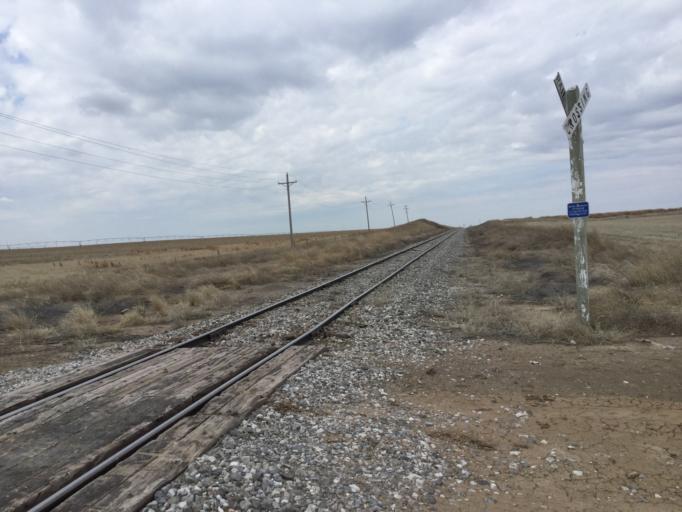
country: US
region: Kansas
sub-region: Stanton County
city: Johnson
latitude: 37.5626
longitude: -101.6532
